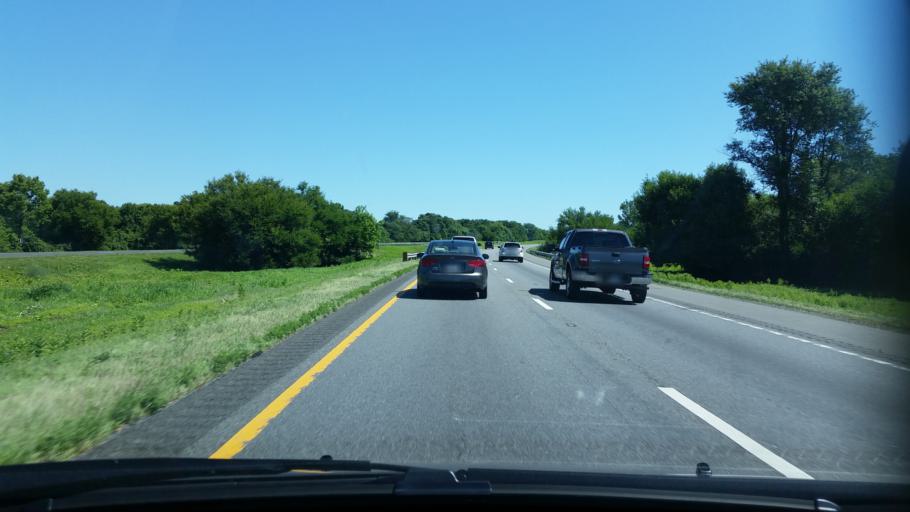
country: US
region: Virginia
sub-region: City of Winchester
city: Winchester
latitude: 39.2305
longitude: -78.1345
